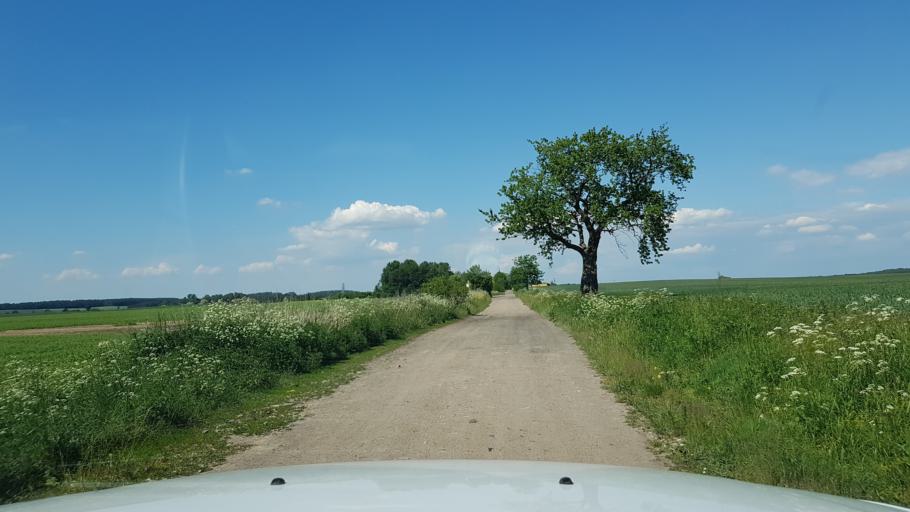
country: PL
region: West Pomeranian Voivodeship
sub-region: Powiat gryfinski
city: Banie
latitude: 53.1277
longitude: 14.5447
